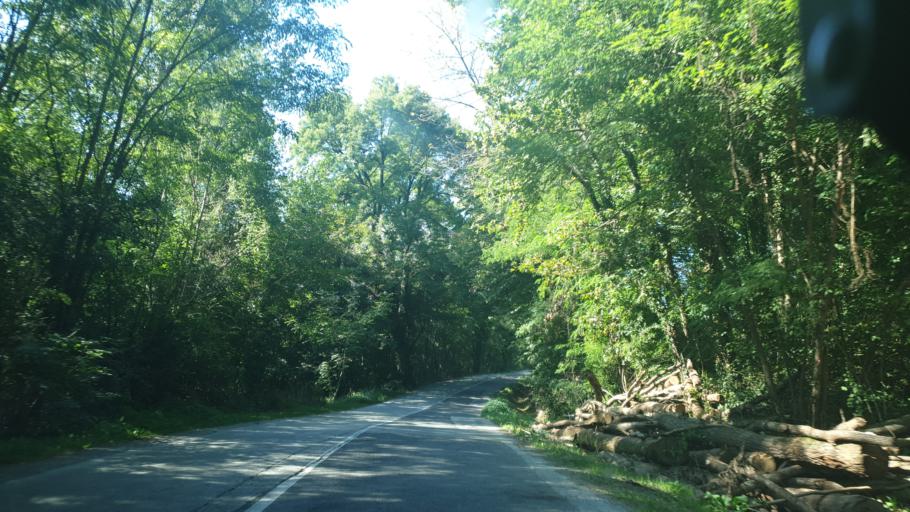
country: RS
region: Central Serbia
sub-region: Kolubarski Okrug
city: Lajkovac
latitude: 44.3213
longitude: 20.1879
